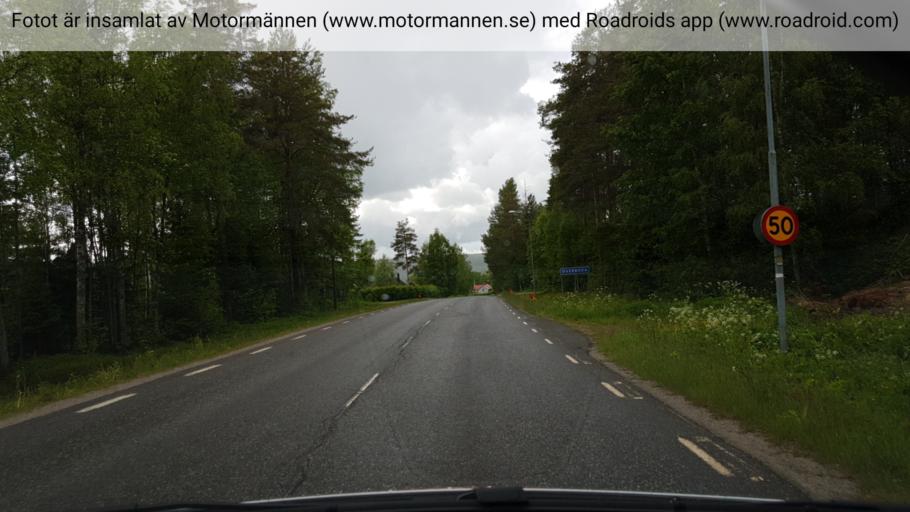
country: SE
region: Vaesterbotten
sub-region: Vannas Kommun
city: Vannasby
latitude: 63.8509
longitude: 19.9360
